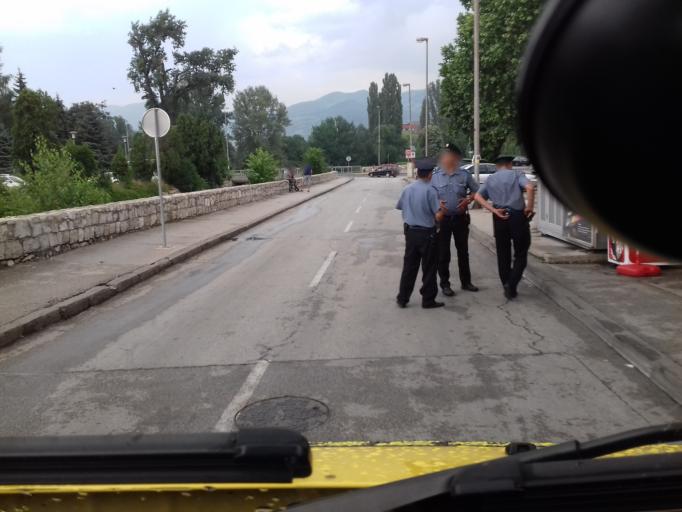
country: BA
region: Federation of Bosnia and Herzegovina
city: Zenica
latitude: 44.1998
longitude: 17.9095
